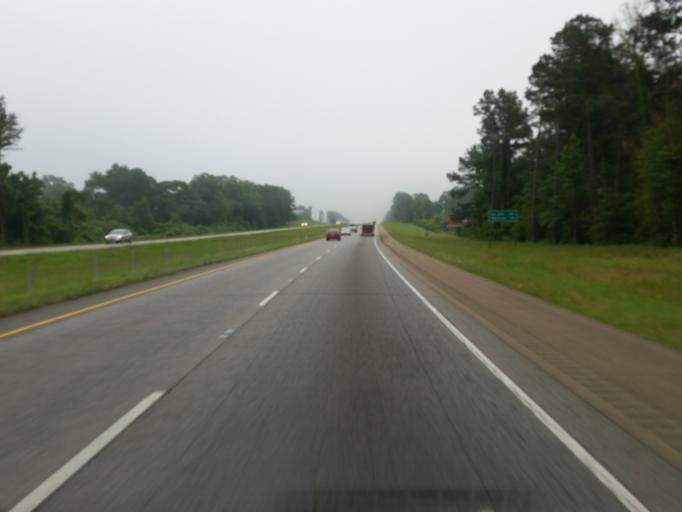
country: US
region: Louisiana
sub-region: Webster Parish
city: Minden
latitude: 32.5873
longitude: -93.2811
